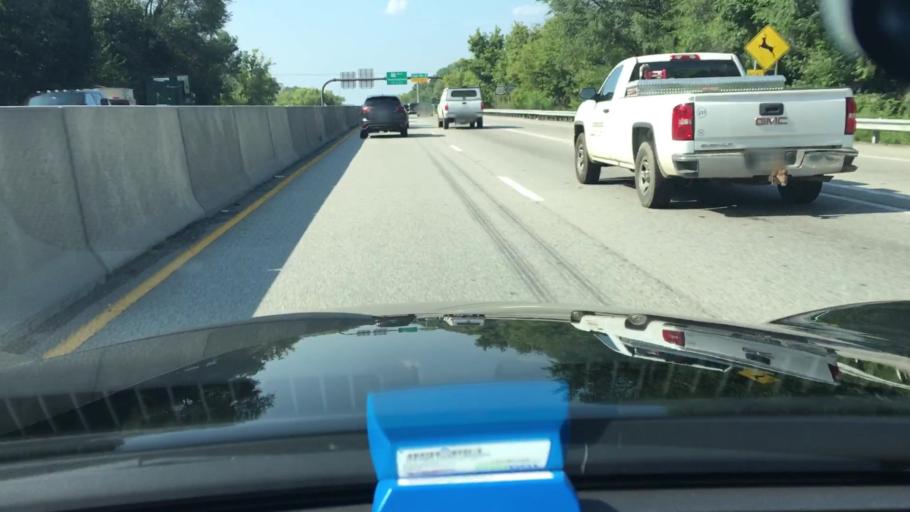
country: US
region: Pennsylvania
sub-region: Chester County
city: West Chester
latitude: 39.9699
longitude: -75.5826
